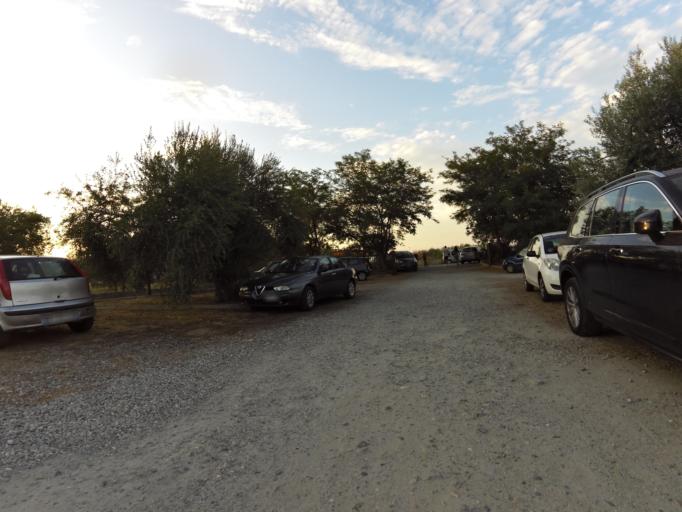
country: IT
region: Calabria
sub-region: Provincia di Reggio Calabria
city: Monasterace Marina
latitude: 38.4507
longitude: 16.5787
